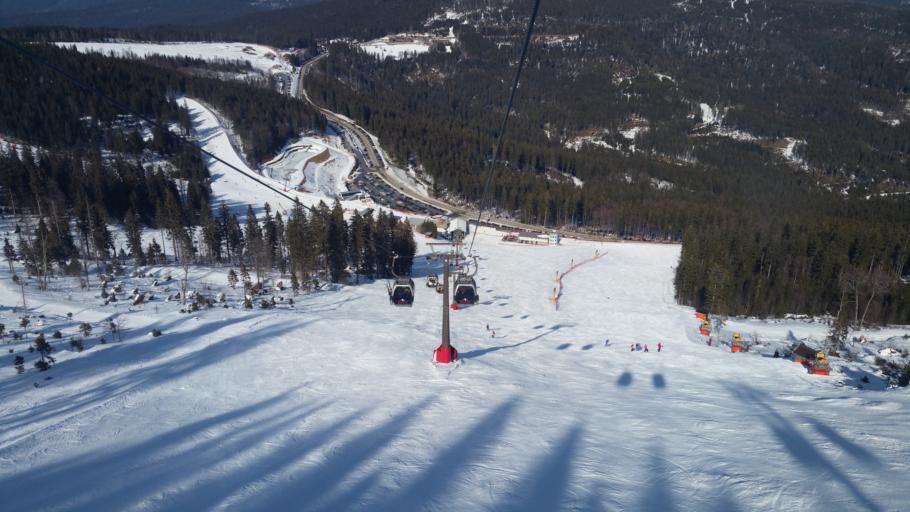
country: DE
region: Bavaria
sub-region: Lower Bavaria
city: Bayerisch Eisenstein
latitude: 49.1156
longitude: 13.1396
